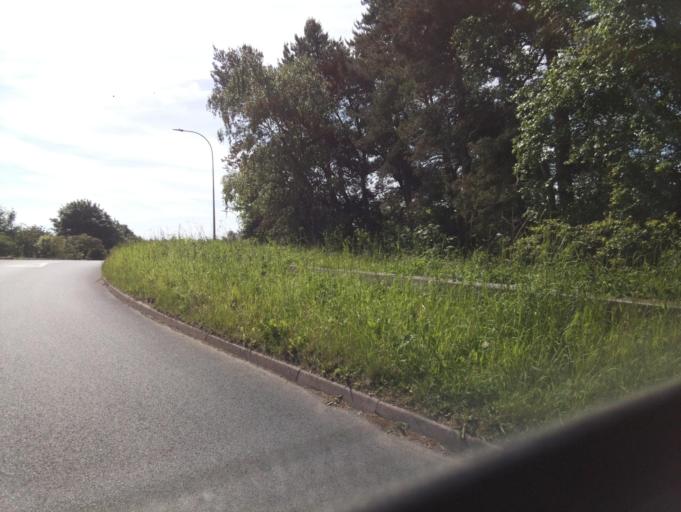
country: GB
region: England
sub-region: North Lincolnshire
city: Broughton
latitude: 53.5552
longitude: -0.5849
